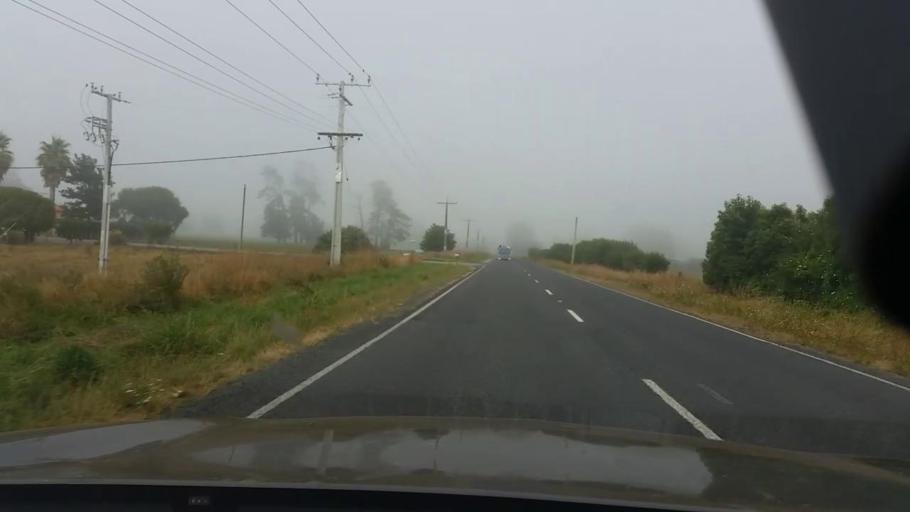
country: NZ
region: Waikato
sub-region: Hamilton City
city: Hamilton
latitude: -37.6349
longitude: 175.3032
